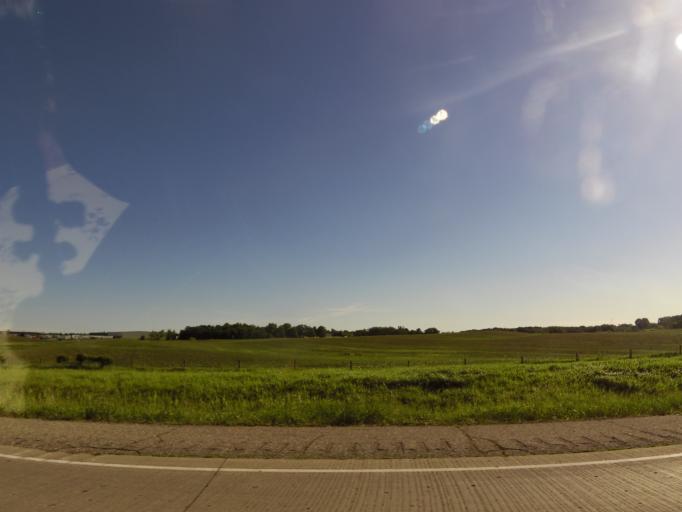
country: US
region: Minnesota
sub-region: Douglas County
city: Alexandria
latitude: 45.8550
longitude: -95.4223
